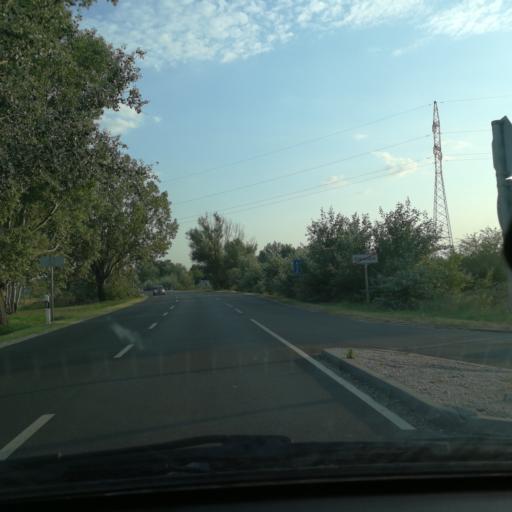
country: HU
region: Bacs-Kiskun
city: Kiskunmajsa
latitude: 46.4899
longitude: 19.7199
